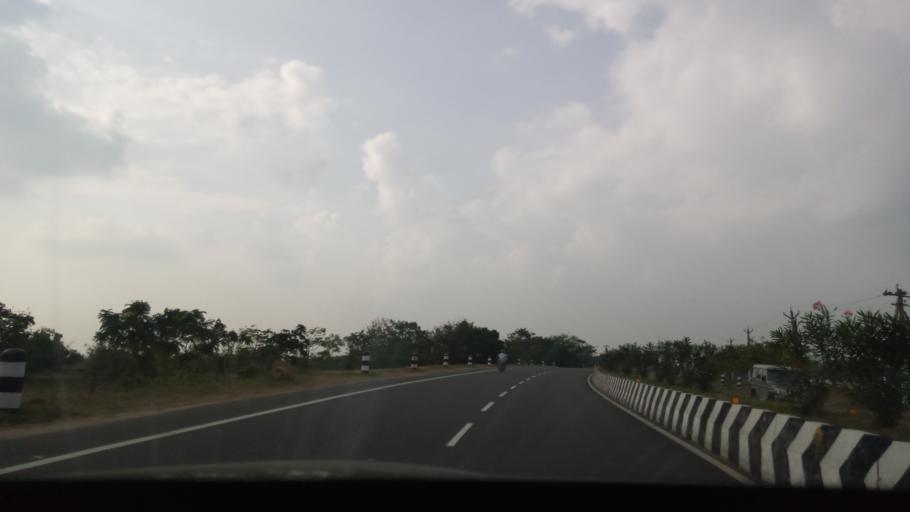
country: IN
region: Tamil Nadu
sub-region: Kancheepuram
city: Injambakkam
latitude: 12.7732
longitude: 80.2490
